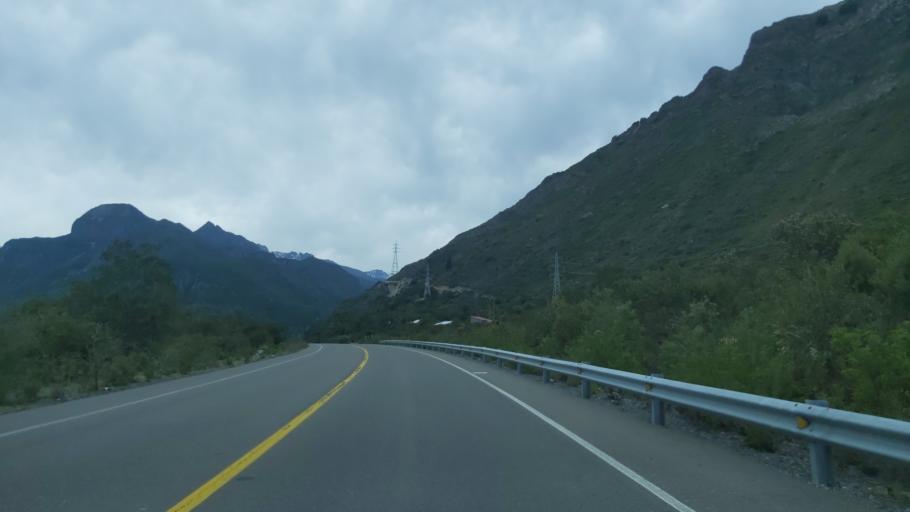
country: CL
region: Maule
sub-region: Provincia de Linares
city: Colbun
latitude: -35.7091
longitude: -71.0925
